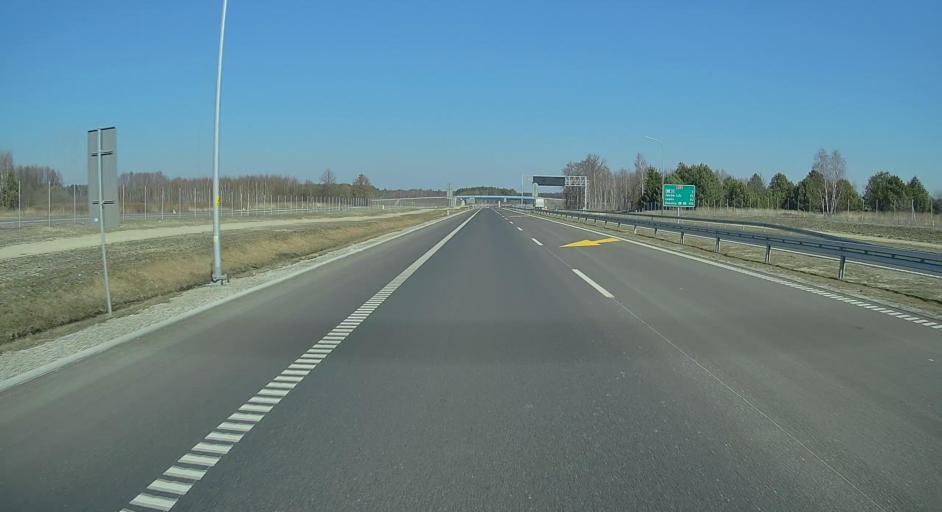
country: PL
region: Subcarpathian Voivodeship
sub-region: Powiat nizanski
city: Jarocin
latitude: 50.5800
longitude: 22.2518
